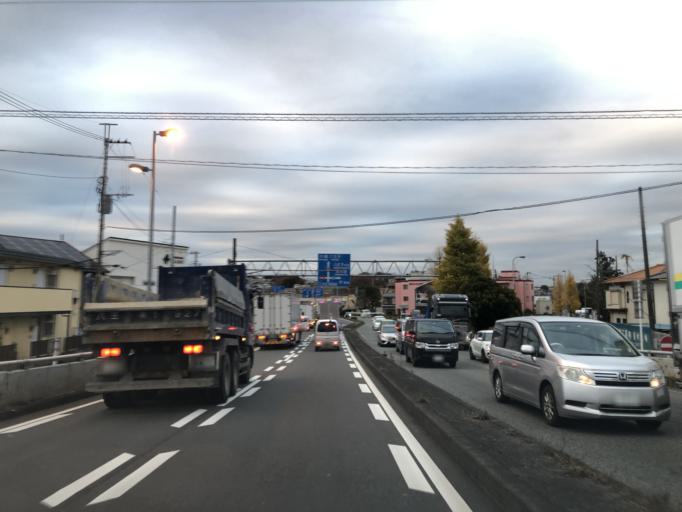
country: JP
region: Tokyo
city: Hachioji
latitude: 35.5995
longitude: 139.3388
